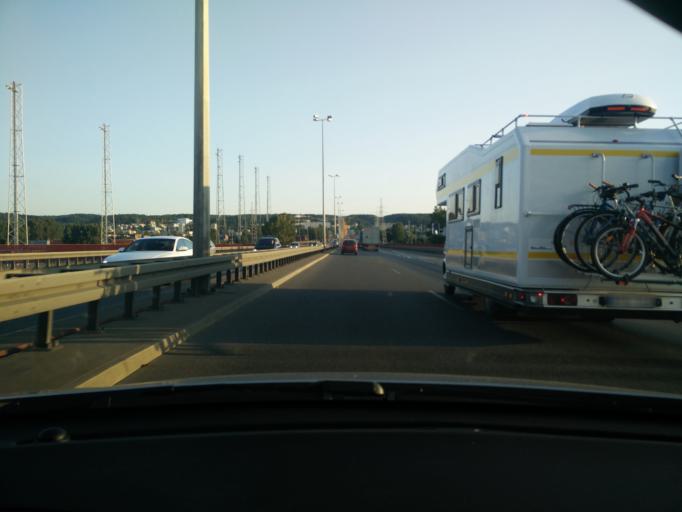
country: PL
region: Pomeranian Voivodeship
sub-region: Gdynia
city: Pogorze
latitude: 54.5448
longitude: 18.5004
